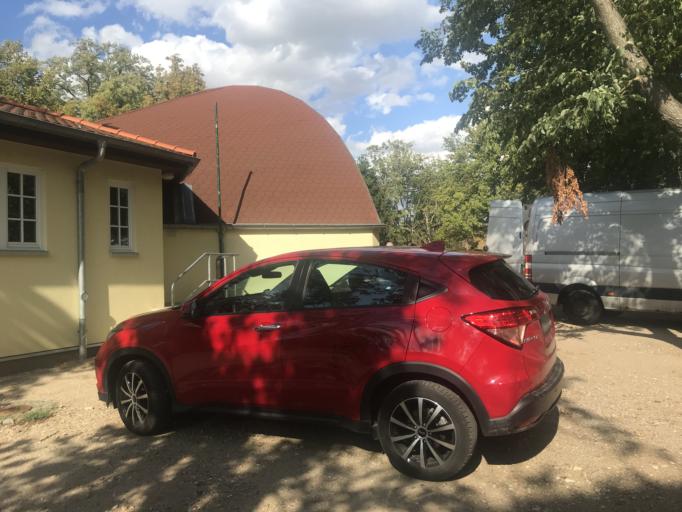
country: DE
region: Saxony-Anhalt
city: Bad Durrenberg
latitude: 51.2936
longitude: 12.0622
